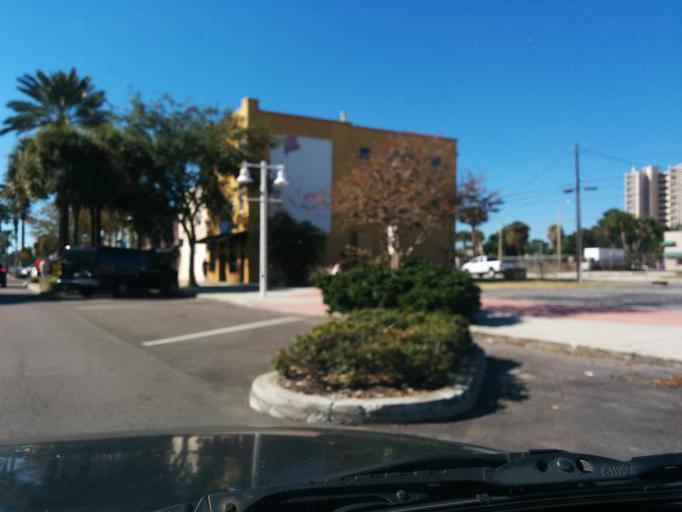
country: US
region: Florida
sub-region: Pinellas County
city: Saint Petersburg
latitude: 27.7712
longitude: -82.6485
